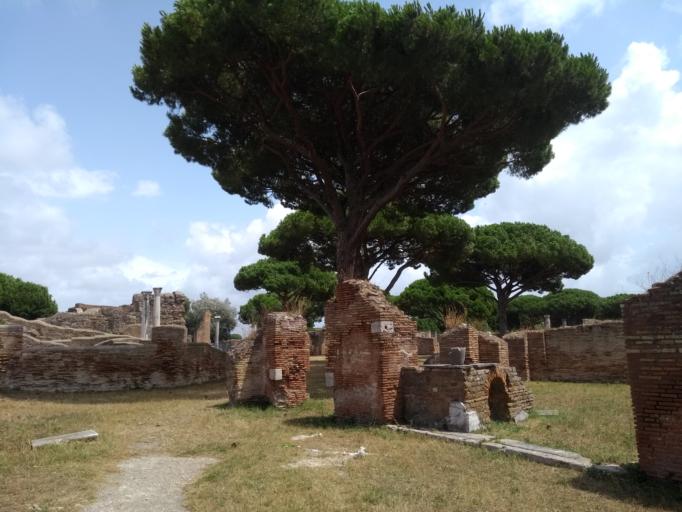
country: IT
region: Latium
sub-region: Citta metropolitana di Roma Capitale
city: Lido di Ostia
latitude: 41.7535
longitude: 12.2888
